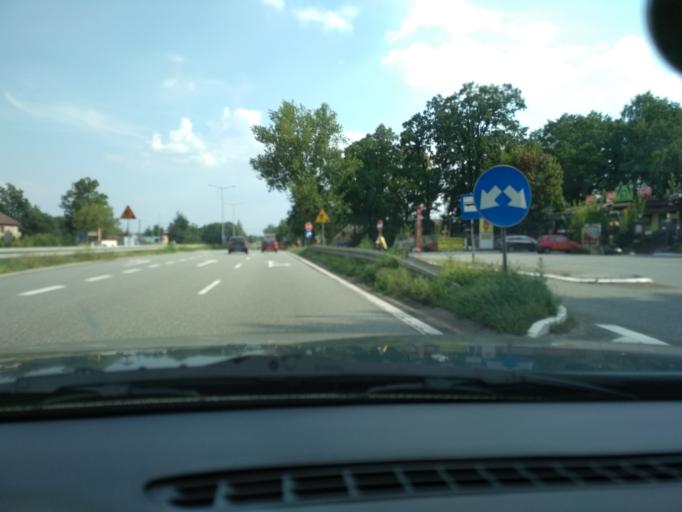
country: PL
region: Silesian Voivodeship
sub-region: Zory
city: Zory
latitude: 50.0111
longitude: 18.7087
